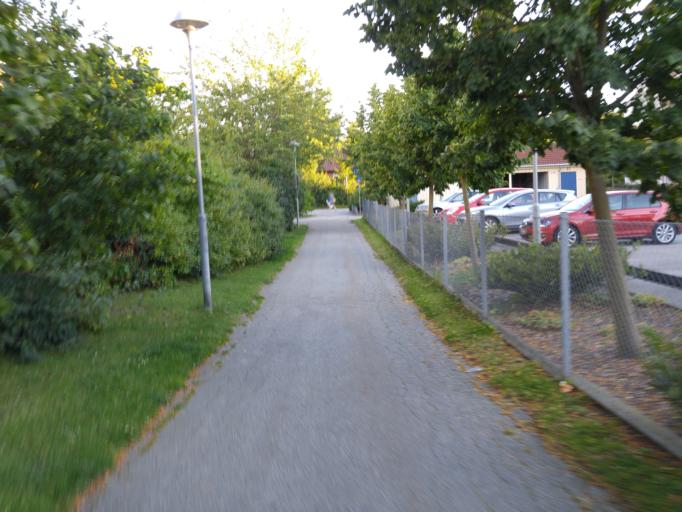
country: SE
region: Skane
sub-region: Lunds Kommun
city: Lund
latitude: 55.7185
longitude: 13.2000
